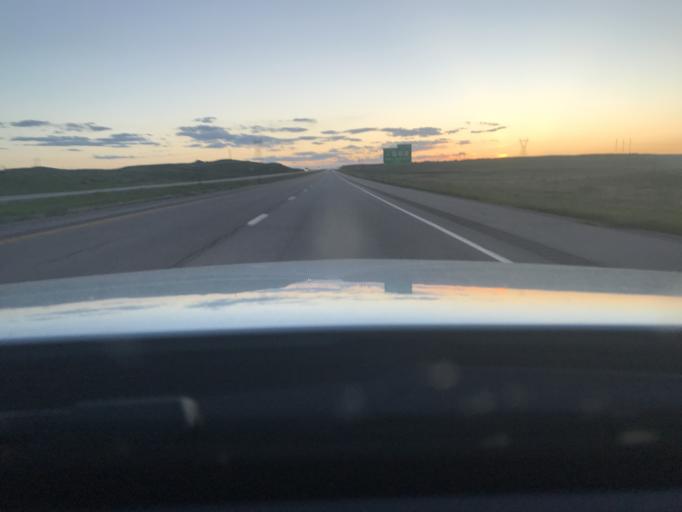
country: US
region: Wyoming
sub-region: Converse County
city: Glenrock
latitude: 42.8202
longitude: -105.7650
